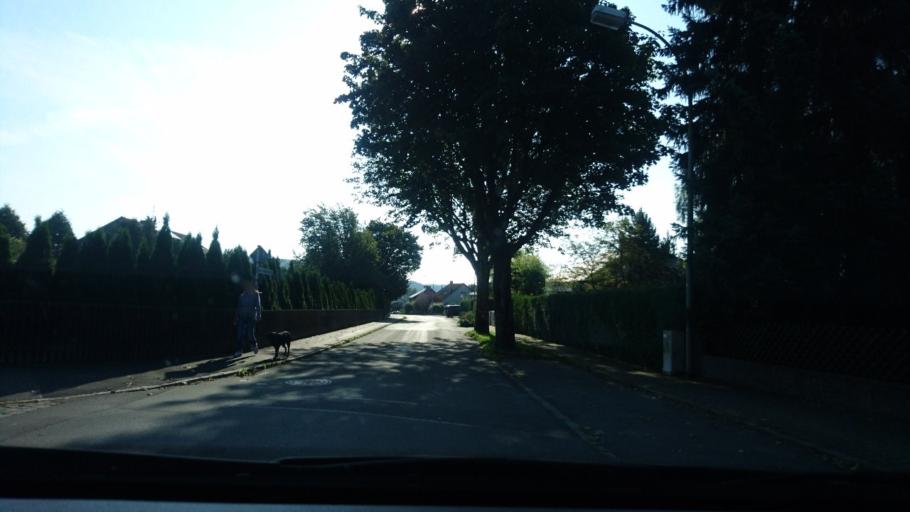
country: DE
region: Bavaria
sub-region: Upper Franconia
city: Naila
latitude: 50.3327
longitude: 11.6961
